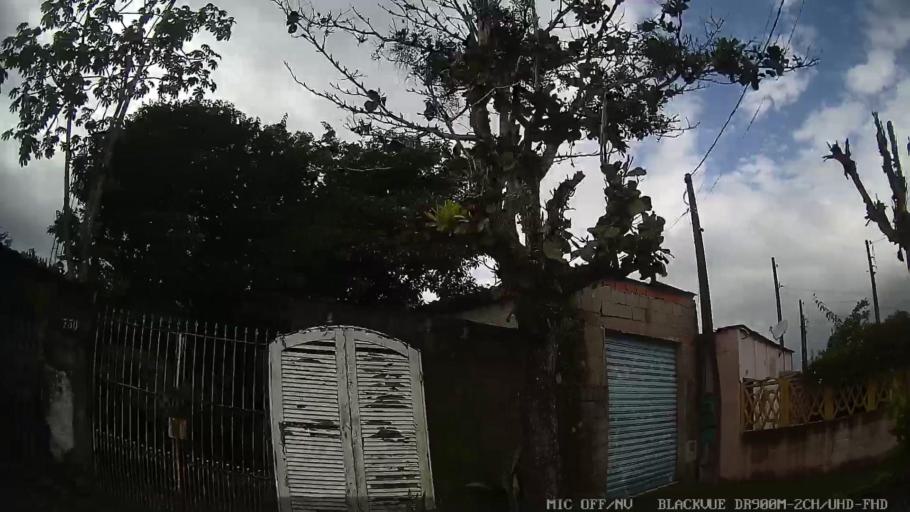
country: BR
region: Sao Paulo
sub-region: Itanhaem
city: Itanhaem
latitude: -24.1862
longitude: -46.8110
